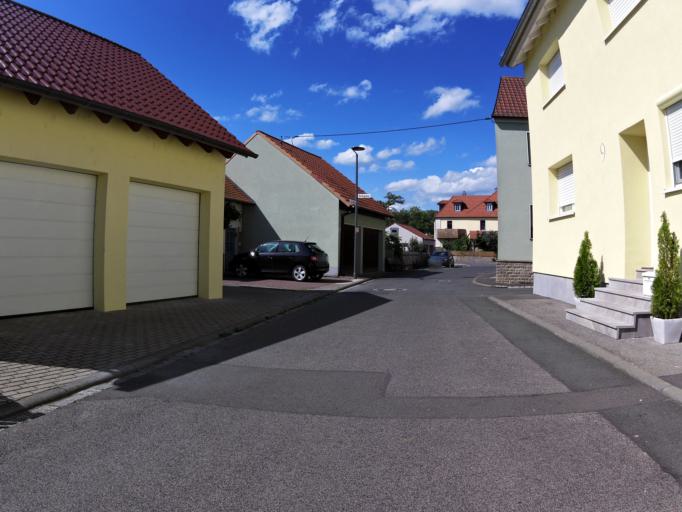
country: DE
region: Bavaria
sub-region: Regierungsbezirk Unterfranken
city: Marktsteft
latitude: 49.6953
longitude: 10.1336
